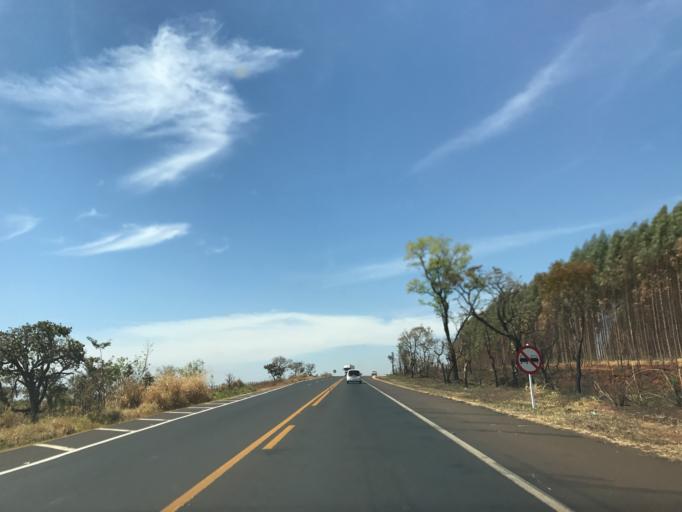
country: BR
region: Minas Gerais
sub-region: Prata
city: Prata
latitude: -19.1119
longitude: -48.9728
